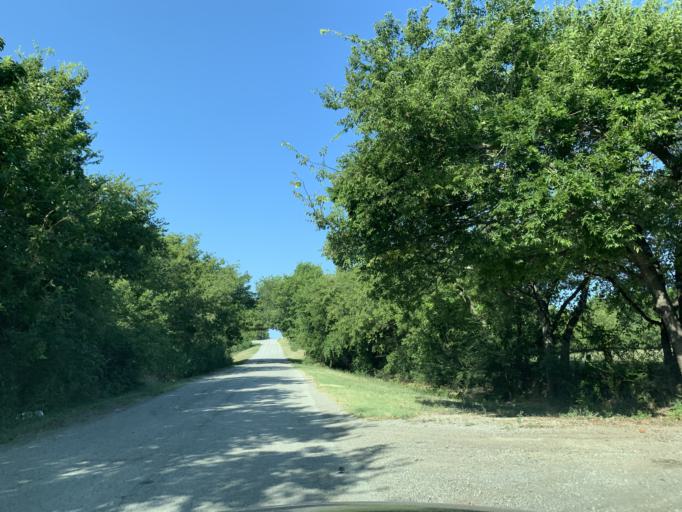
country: US
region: Texas
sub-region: Dallas County
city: Hutchins
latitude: 32.6629
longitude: -96.7440
